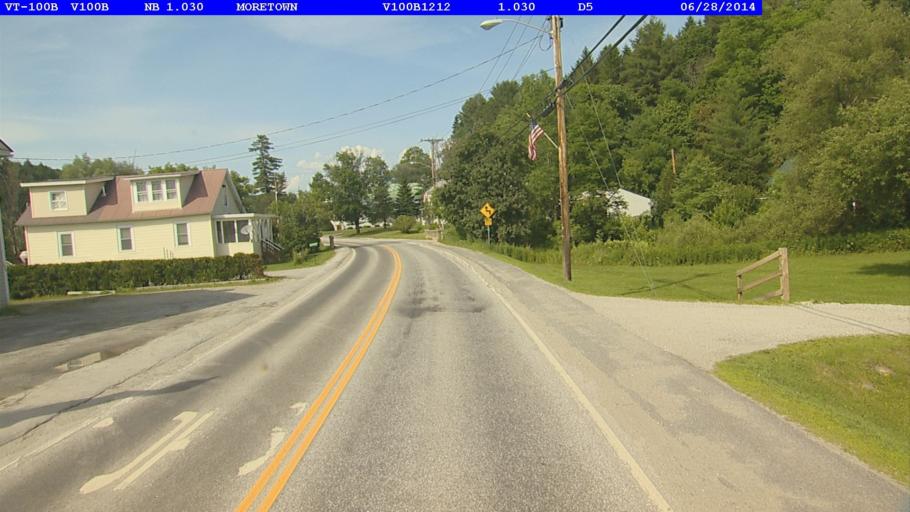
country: US
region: Vermont
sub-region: Washington County
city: Waterbury
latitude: 44.2491
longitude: -72.7619
